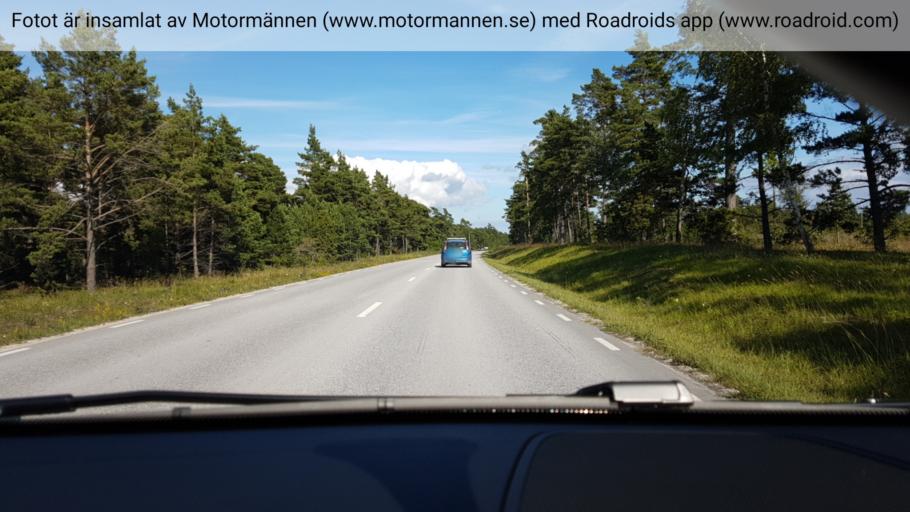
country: SE
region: Gotland
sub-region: Gotland
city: Slite
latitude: 57.7472
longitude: 18.6647
